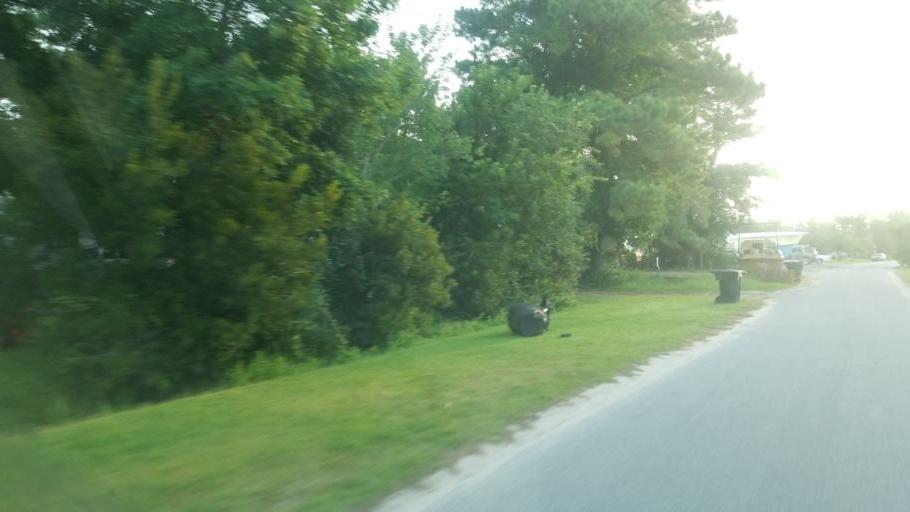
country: US
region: North Carolina
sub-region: Dare County
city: Wanchese
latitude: 35.8411
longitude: -75.6324
